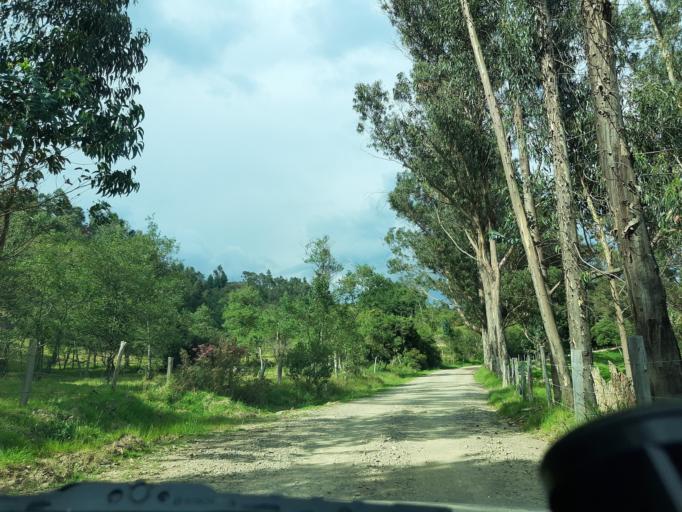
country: CO
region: Boyaca
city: Raquira
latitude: 5.5106
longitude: -73.6671
